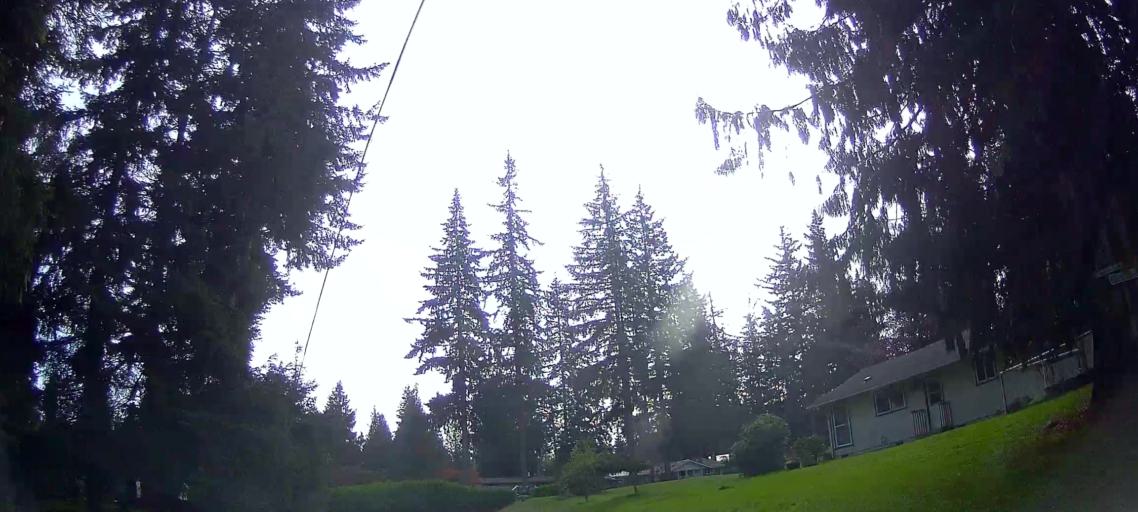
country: US
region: Washington
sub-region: Snohomish County
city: Stanwood
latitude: 48.2877
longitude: -122.3442
